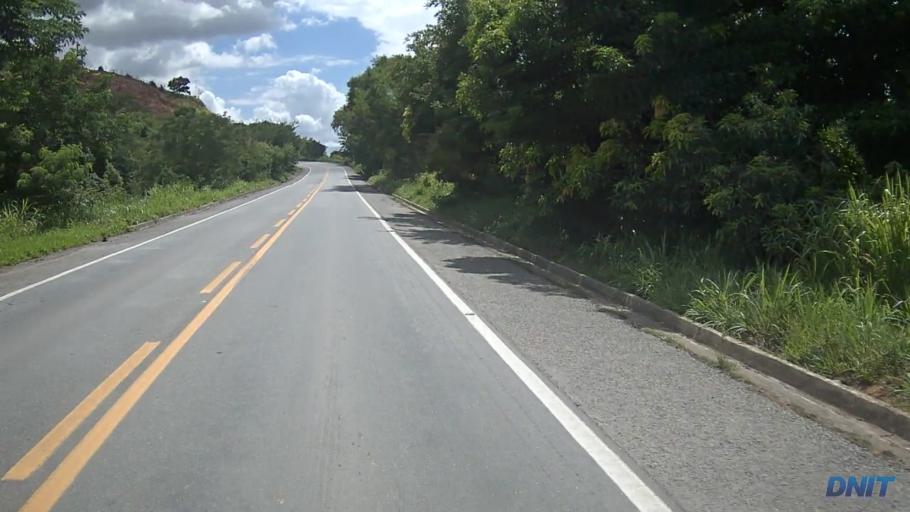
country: BR
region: Minas Gerais
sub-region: Governador Valadares
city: Governador Valadares
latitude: -18.9633
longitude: -42.0783
